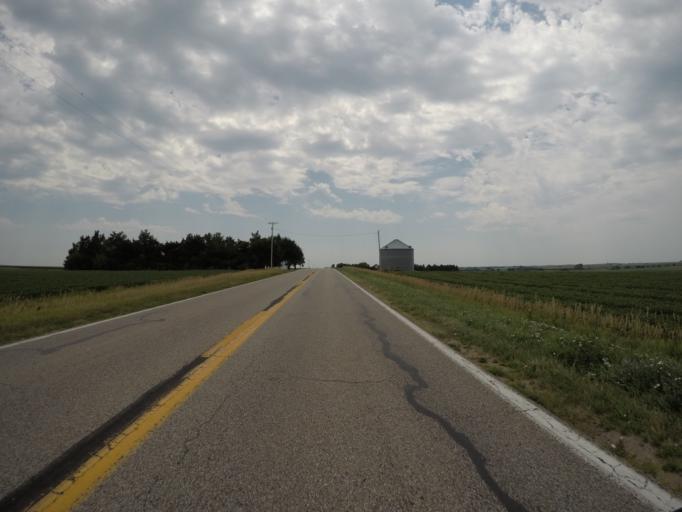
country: US
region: Nebraska
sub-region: Adams County
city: Hastings
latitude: 40.6065
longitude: -98.5732
